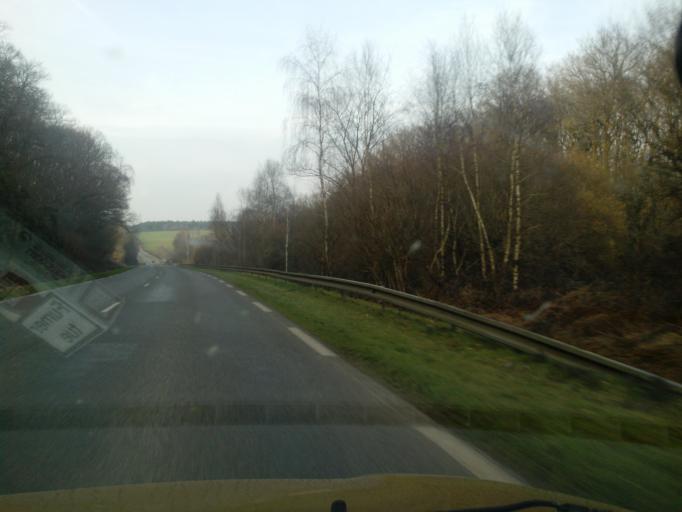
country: FR
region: Brittany
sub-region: Departement du Morbihan
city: Molac
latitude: 47.6991
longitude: -2.4446
